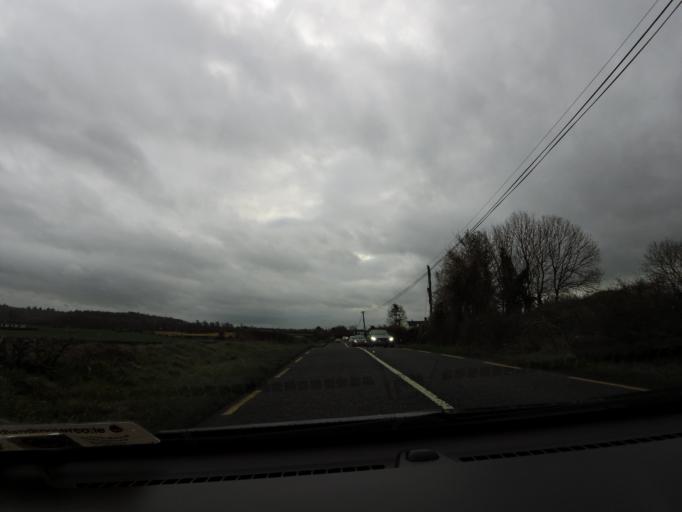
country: IE
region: Leinster
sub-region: Kilkenny
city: Ballyragget
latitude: 52.7272
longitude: -7.3077
